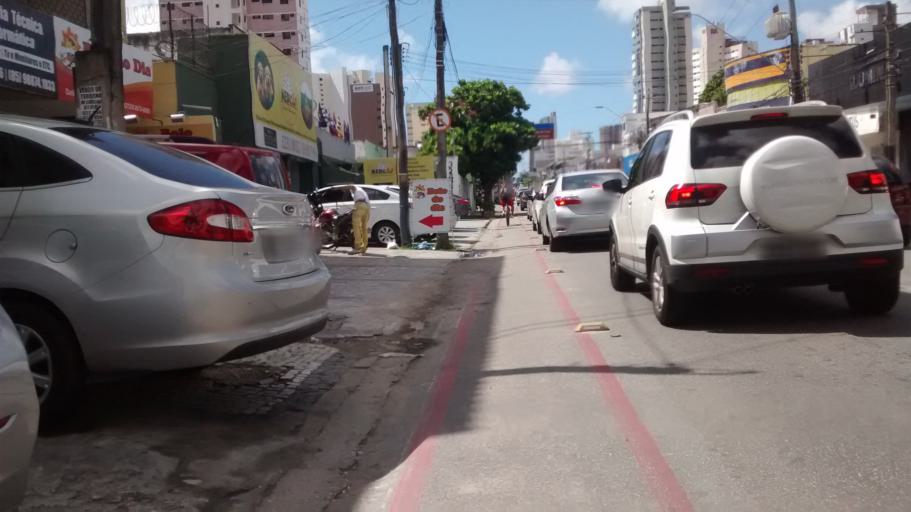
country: BR
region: Ceara
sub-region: Fortaleza
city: Fortaleza
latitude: -3.7413
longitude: -38.5156
